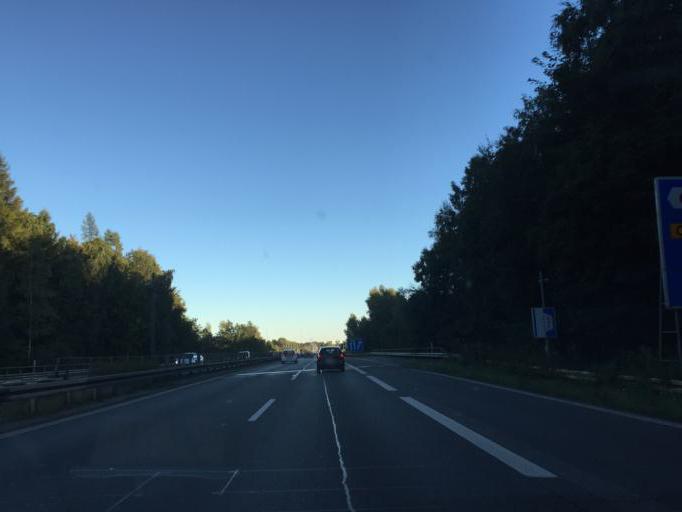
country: DK
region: Capital Region
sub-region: Herlev Kommune
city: Herlev
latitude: 55.7679
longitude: 12.4281
